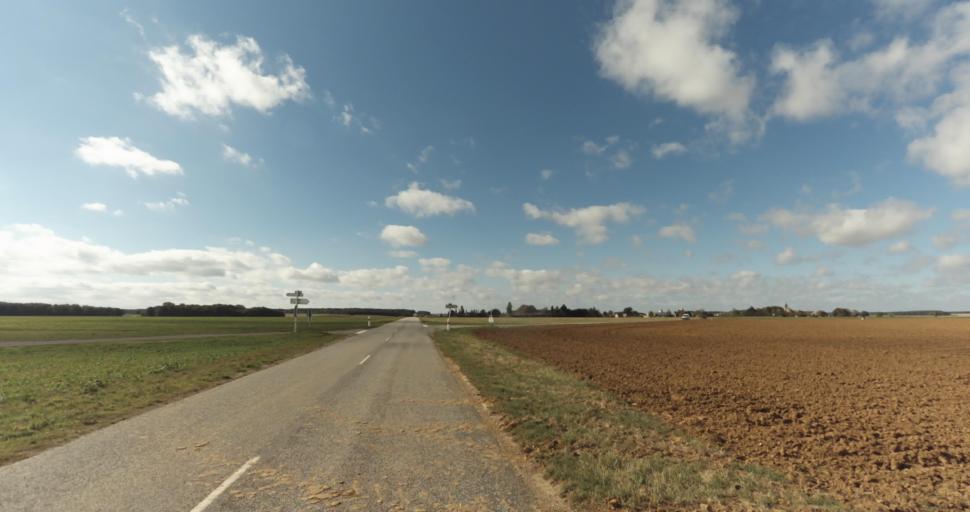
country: FR
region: Centre
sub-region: Departement d'Eure-et-Loir
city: Treon
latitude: 48.7035
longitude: 1.2965
